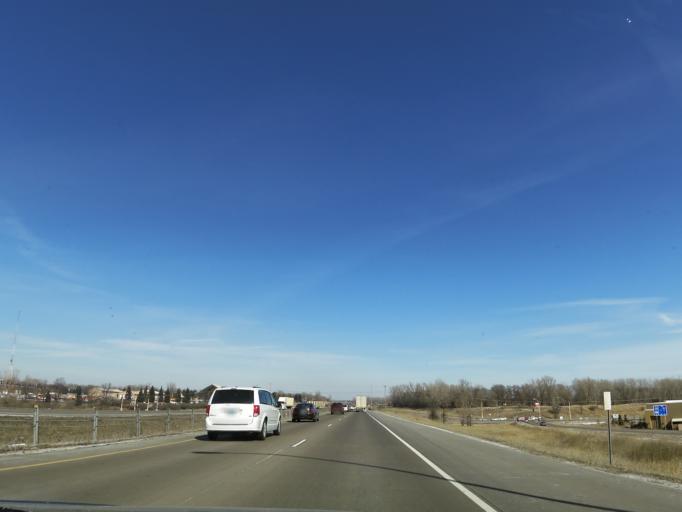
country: US
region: Minnesota
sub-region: Washington County
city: Oakdale
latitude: 44.9951
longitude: -92.9597
